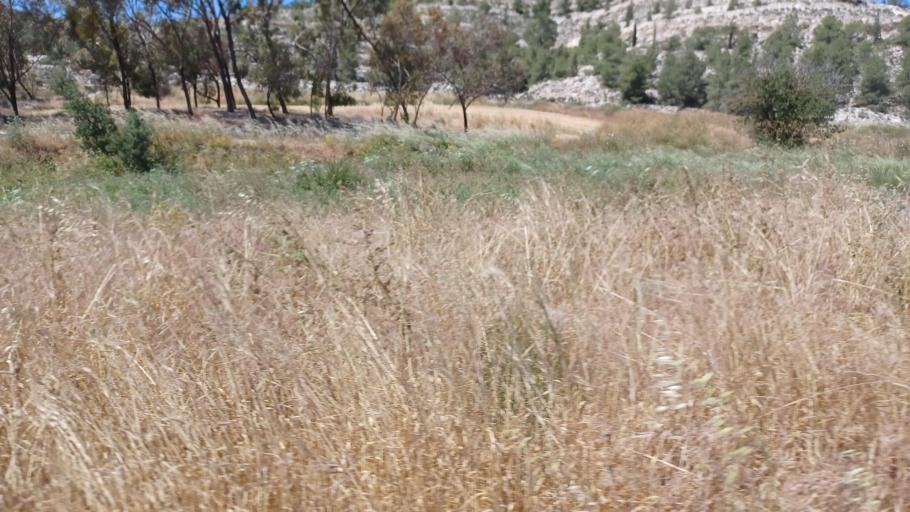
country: CY
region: Lefkosia
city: Lympia
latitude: 34.9929
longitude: 33.5279
